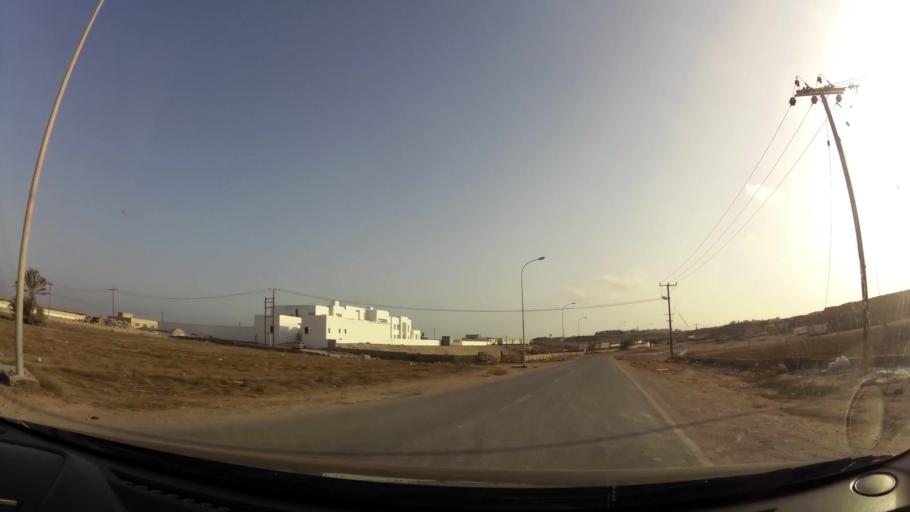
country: OM
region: Zufar
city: Salalah
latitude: 16.9970
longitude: 54.0216
